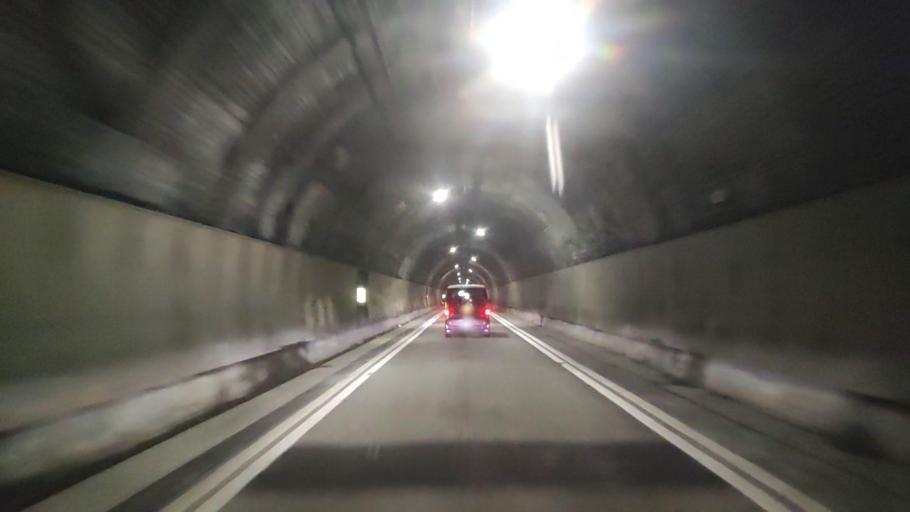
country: JP
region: Fukui
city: Takefu
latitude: 35.8437
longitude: 136.1240
